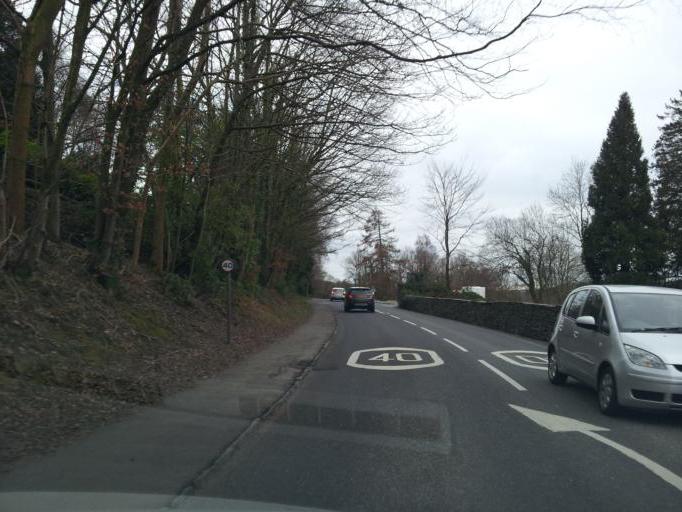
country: GB
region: England
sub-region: Cumbria
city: Windermere
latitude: 54.3846
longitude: -2.9168
